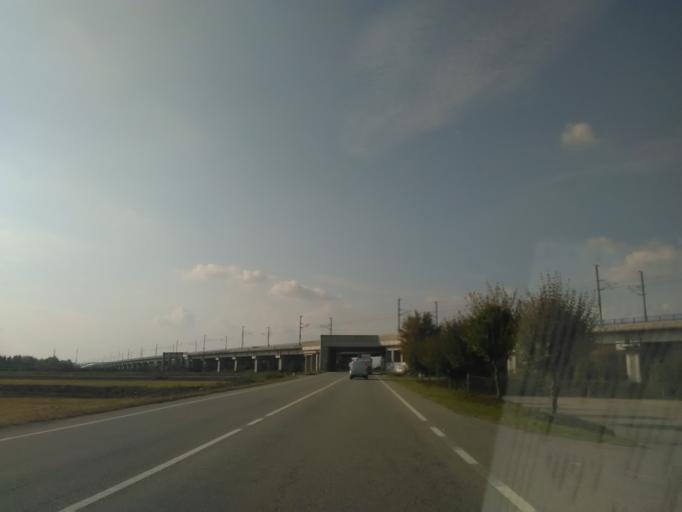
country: IT
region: Piedmont
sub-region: Provincia di Vercelli
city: Balocco
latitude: 45.4391
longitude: 8.2455
